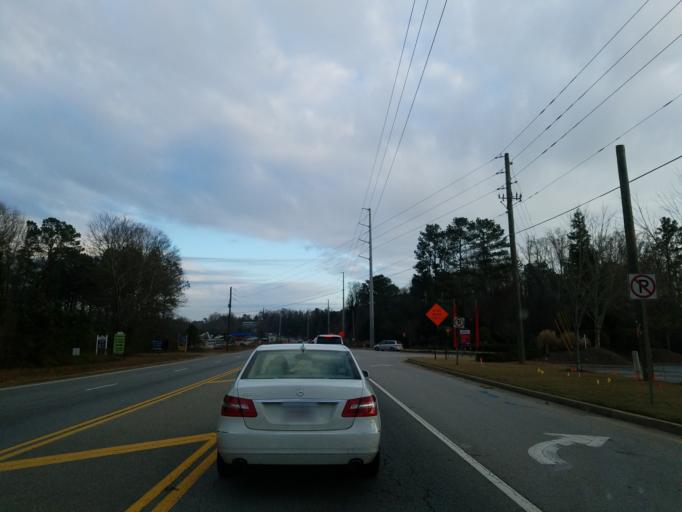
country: US
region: Georgia
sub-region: Forsyth County
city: Cumming
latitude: 34.2684
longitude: -84.0936
